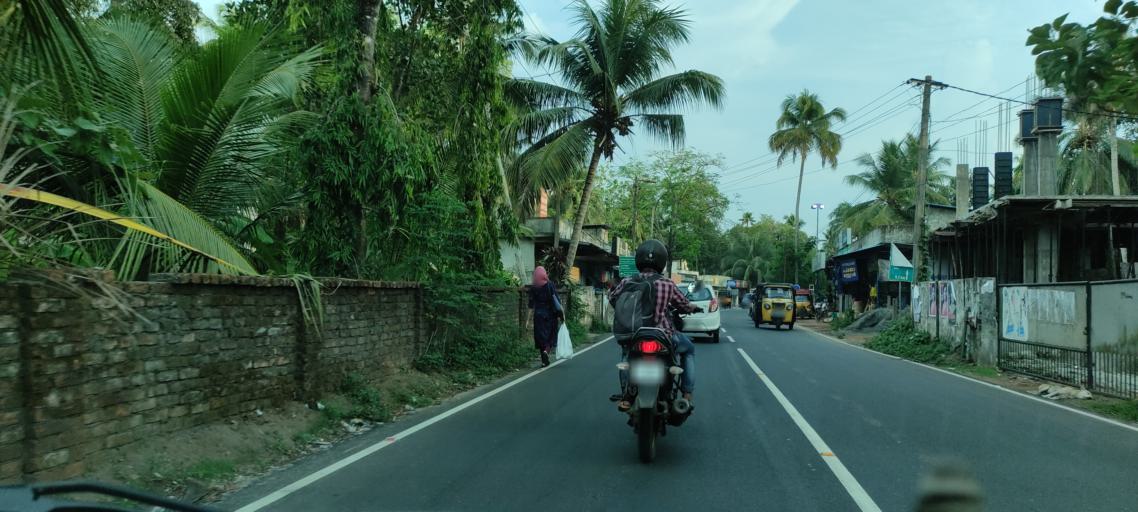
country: IN
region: Kerala
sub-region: Alappuzha
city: Arukutti
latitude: 9.8630
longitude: 76.3237
